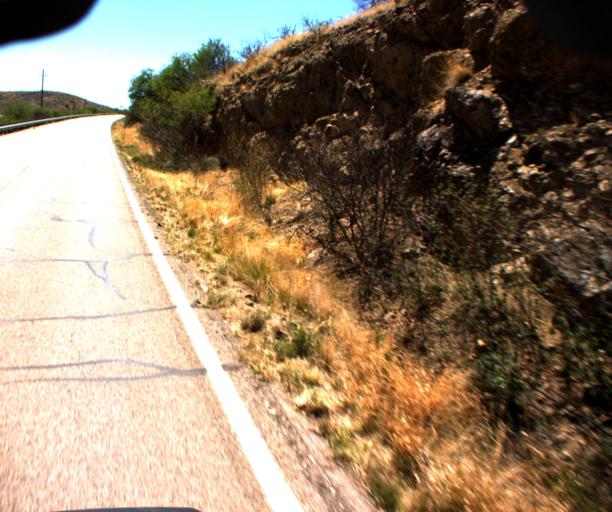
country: US
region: Arizona
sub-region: Pima County
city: Corona de Tucson
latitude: 31.8946
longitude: -110.6662
